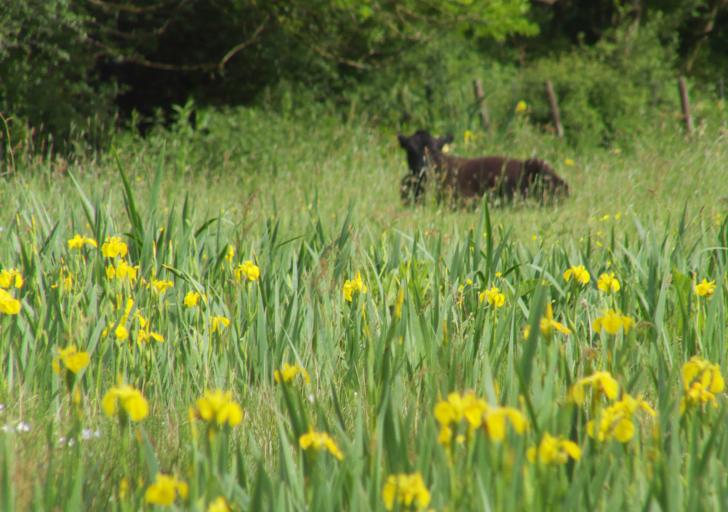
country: GB
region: England
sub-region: Cornwall
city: Wadebridge
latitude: 50.4938
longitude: -4.8028
